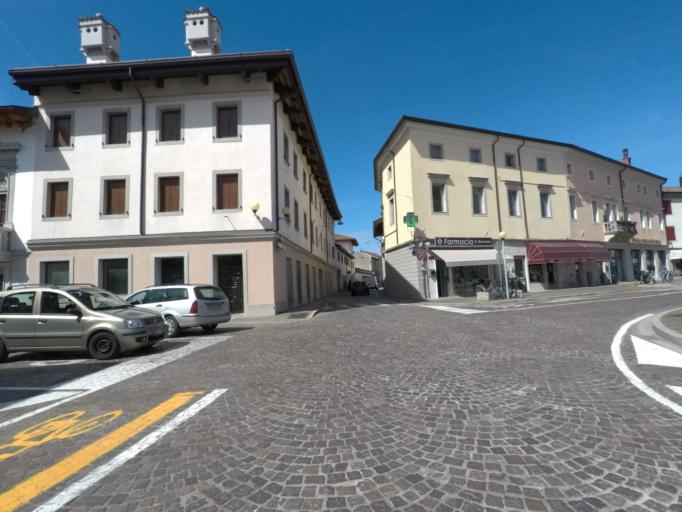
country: IT
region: Friuli Venezia Giulia
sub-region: Provincia di Udine
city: Codroipo
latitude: 45.9614
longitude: 12.9772
